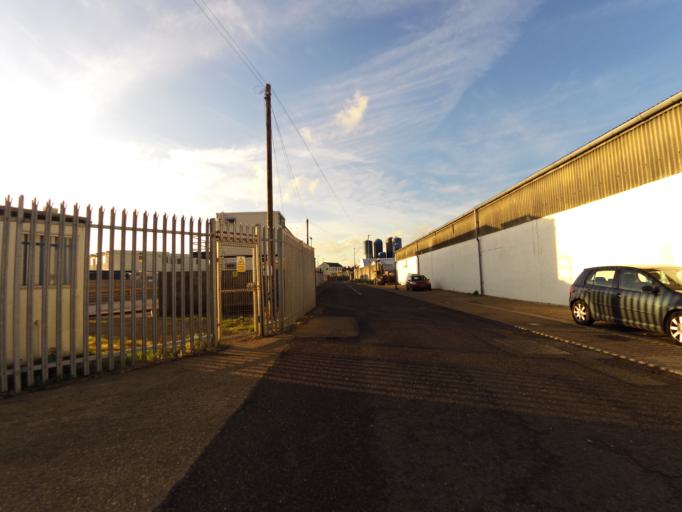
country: GB
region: England
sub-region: Norfolk
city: Gorleston-on-Sea
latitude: 52.5893
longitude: 1.7270
